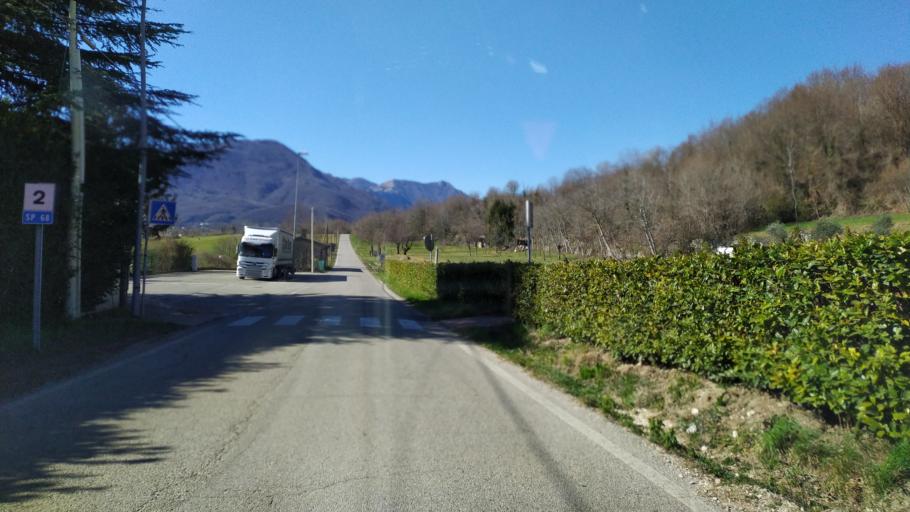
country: IT
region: Veneto
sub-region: Provincia di Vicenza
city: Chiuppano
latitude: 45.7658
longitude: 11.4809
